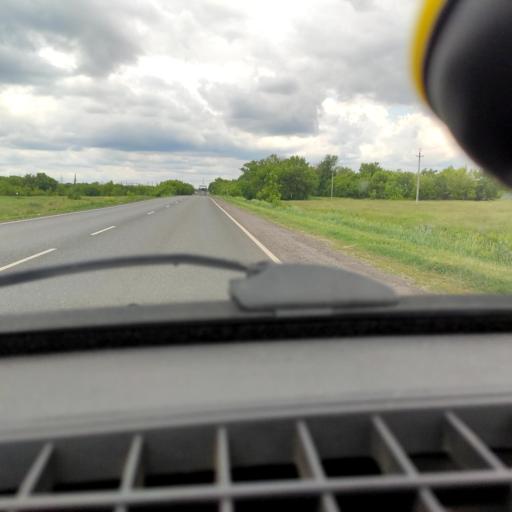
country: RU
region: Samara
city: Povolzhskiy
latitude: 53.6483
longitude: 49.6797
